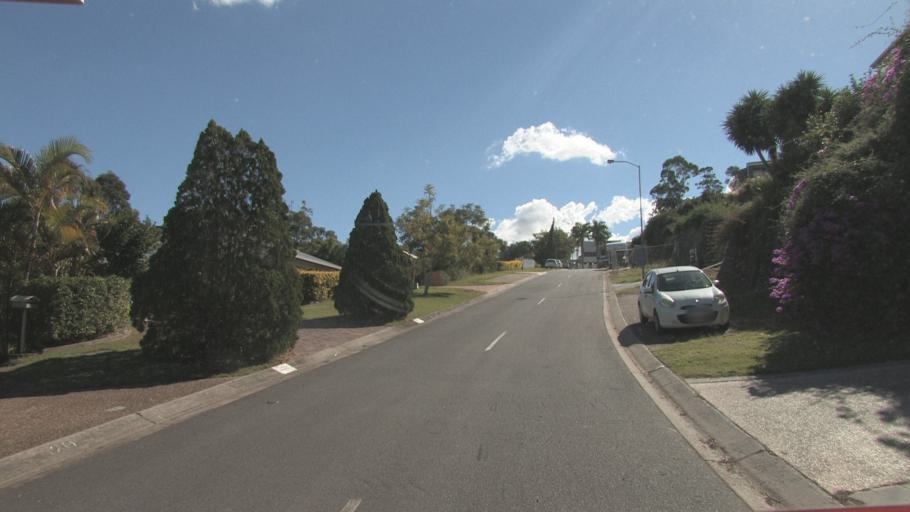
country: AU
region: Queensland
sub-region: Logan
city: Slacks Creek
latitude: -27.6602
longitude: 153.1936
